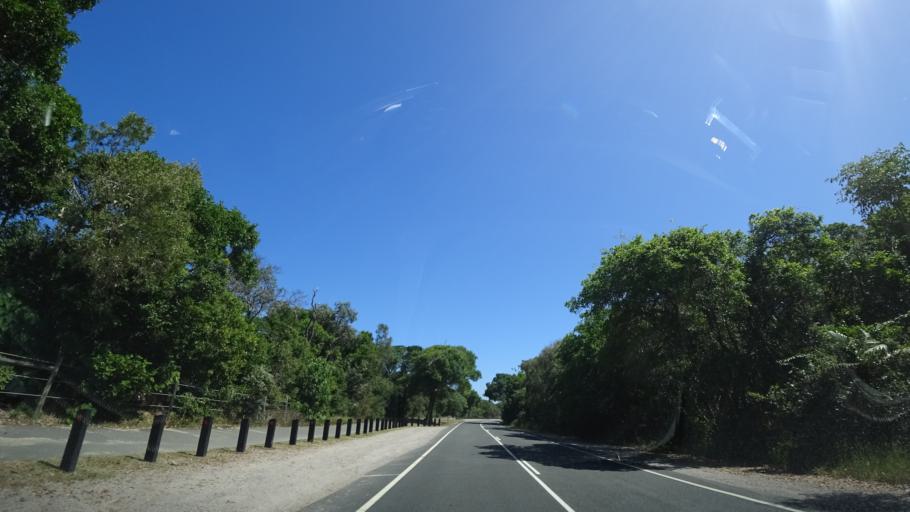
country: AU
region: Queensland
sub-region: Sunshine Coast
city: Mooloolaba
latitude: -26.6259
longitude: 153.1003
